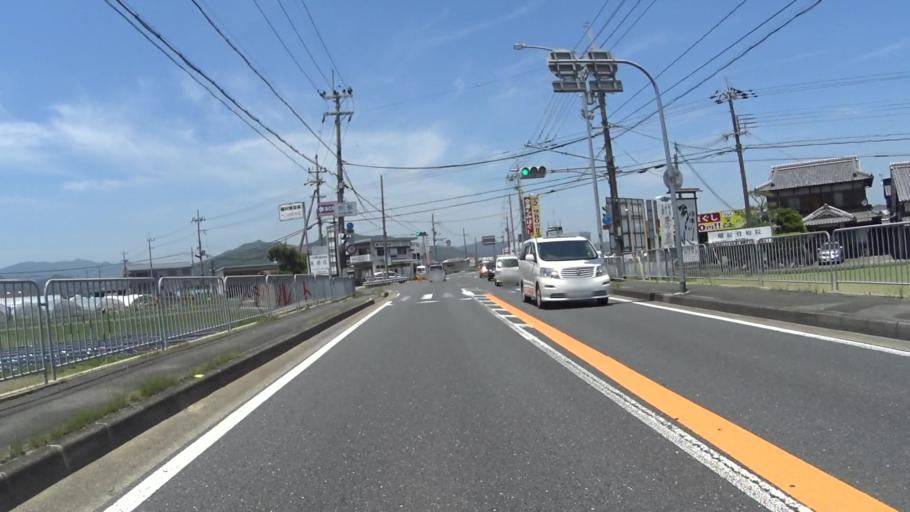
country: JP
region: Kyoto
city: Kameoka
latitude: 35.0176
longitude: 135.5635
